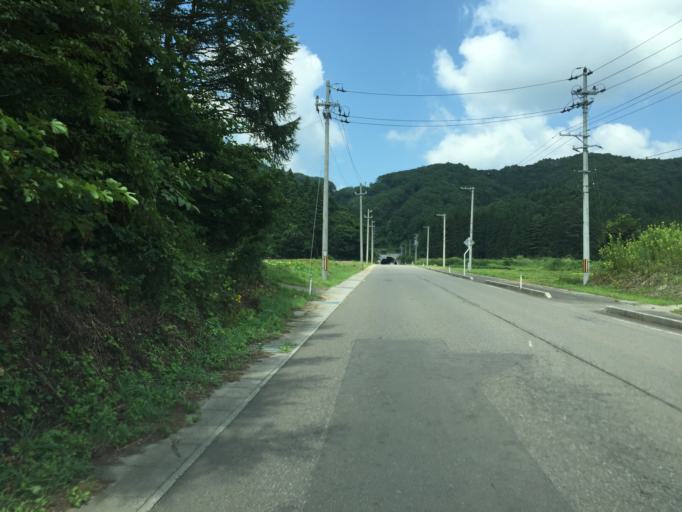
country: JP
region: Fukushima
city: Inawashiro
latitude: 37.4097
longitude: 140.0579
